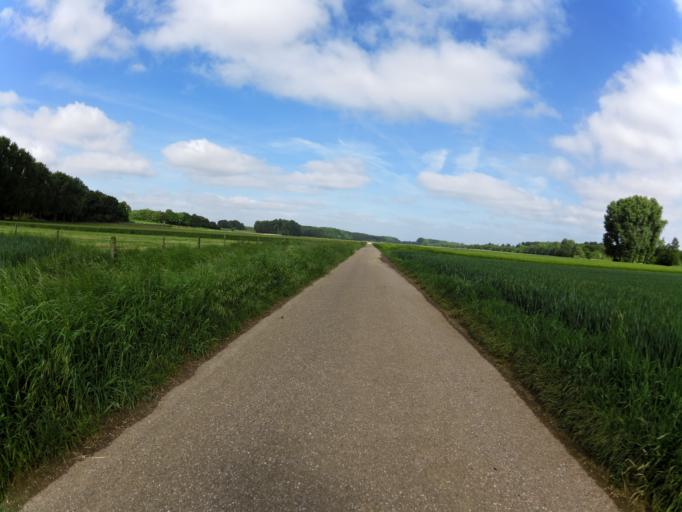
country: DE
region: North Rhine-Westphalia
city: Huckelhoven
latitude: 51.0161
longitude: 6.2194
